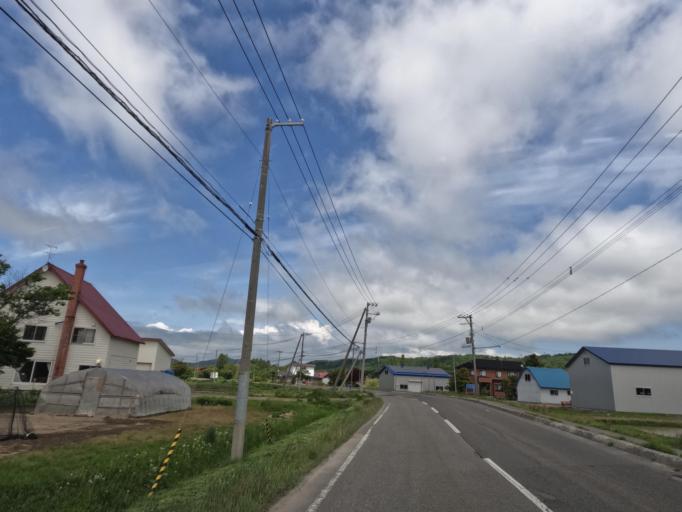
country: JP
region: Hokkaido
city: Tobetsu
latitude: 43.2743
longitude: 141.5334
